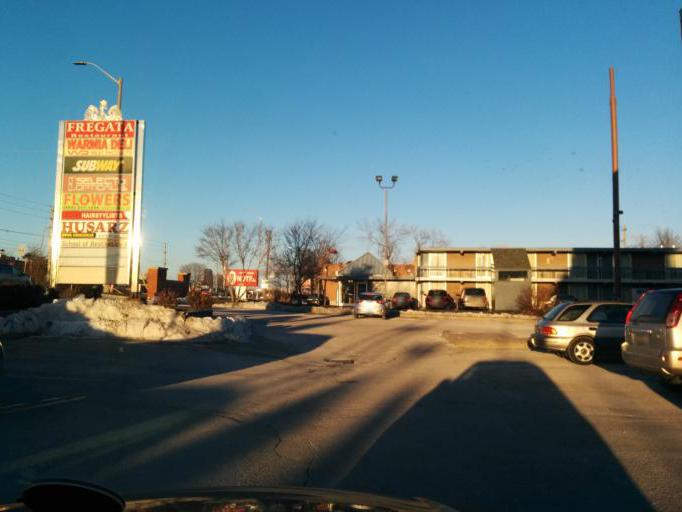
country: CA
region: Ontario
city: Etobicoke
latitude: 43.6200
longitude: -79.5719
